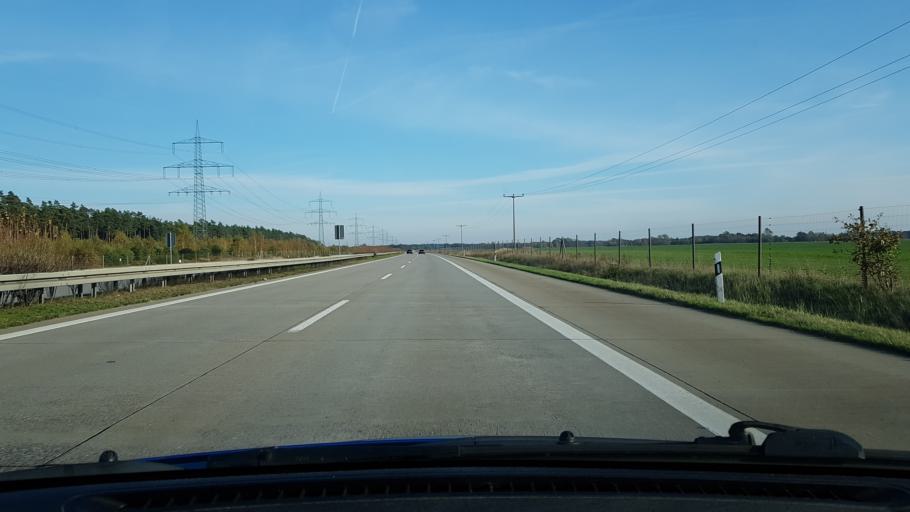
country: DE
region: Mecklenburg-Vorpommern
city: Zarrentin
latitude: 53.5112
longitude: 10.9117
